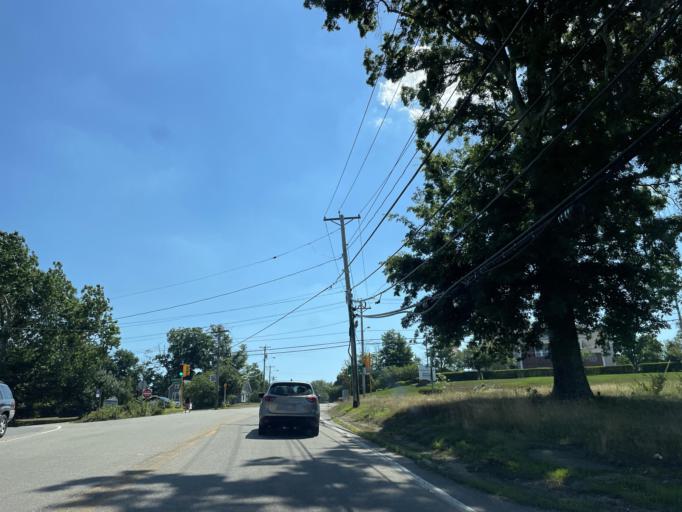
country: US
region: Massachusetts
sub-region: Worcester County
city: Mendon
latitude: 42.1082
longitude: -71.5532
